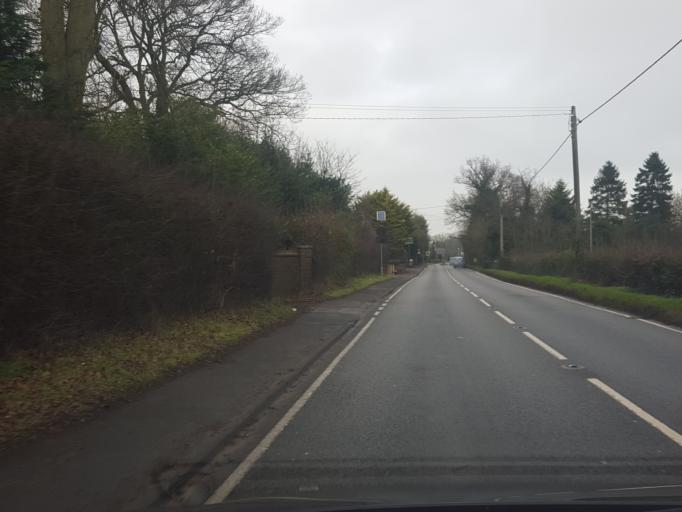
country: GB
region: England
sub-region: Essex
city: Great Horkesley
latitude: 51.9362
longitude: 0.8758
